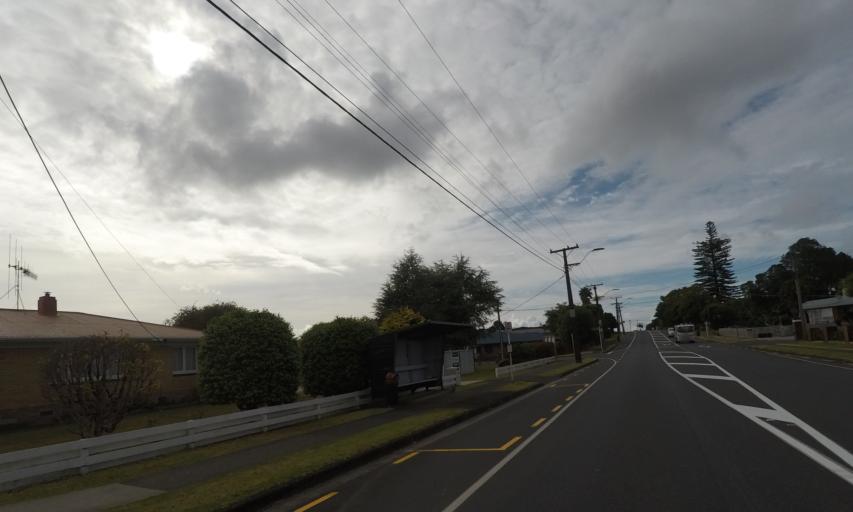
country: NZ
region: Northland
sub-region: Whangarei
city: Whangarei
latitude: -35.6881
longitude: 174.3035
